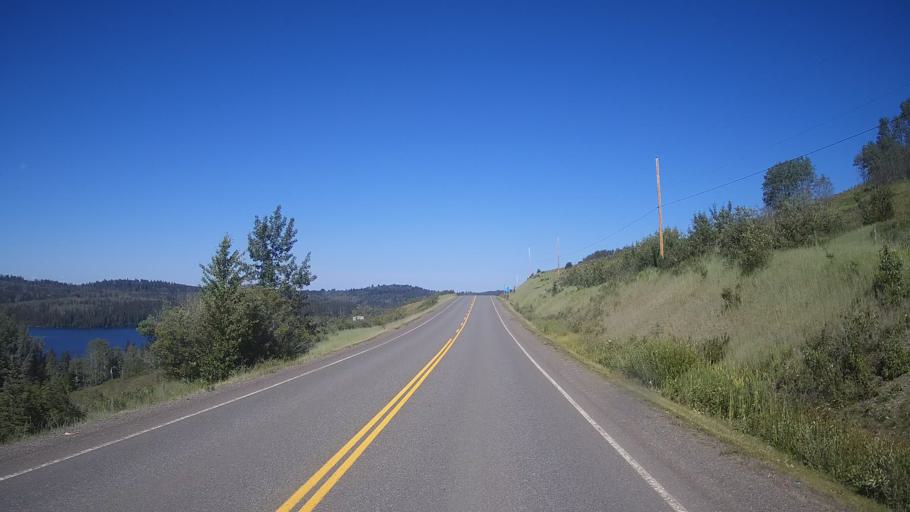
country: CA
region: British Columbia
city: Kamloops
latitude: 51.4974
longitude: -120.5851
